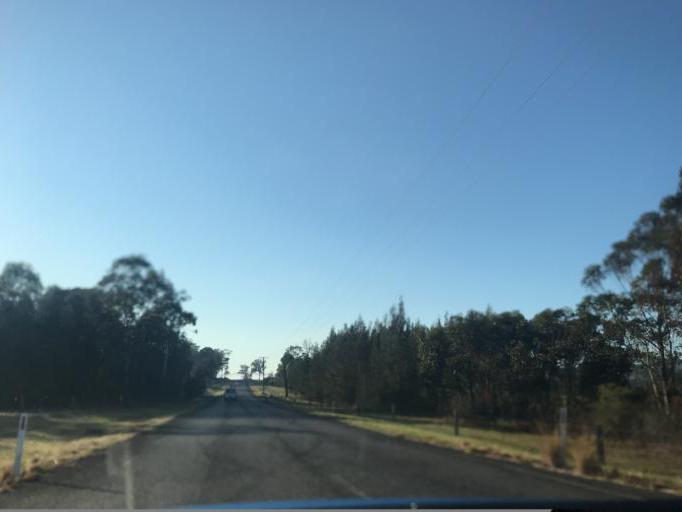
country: AU
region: New South Wales
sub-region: Cessnock
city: Cessnock
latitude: -32.9101
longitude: 151.2944
